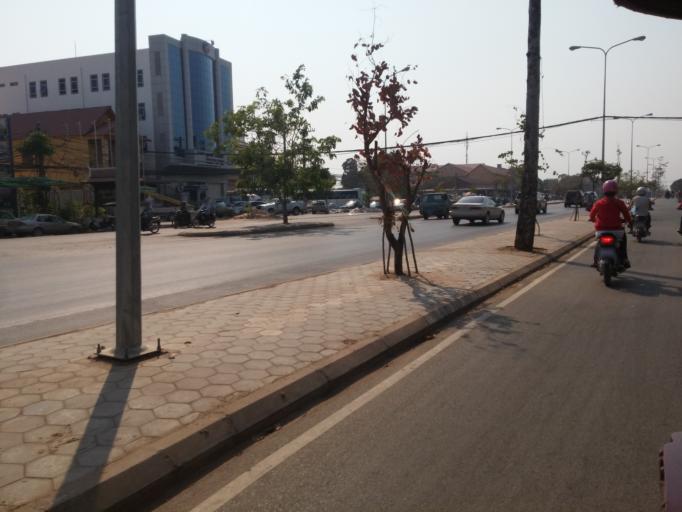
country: KH
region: Siem Reap
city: Siem Reap
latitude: 13.3667
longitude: 103.8503
